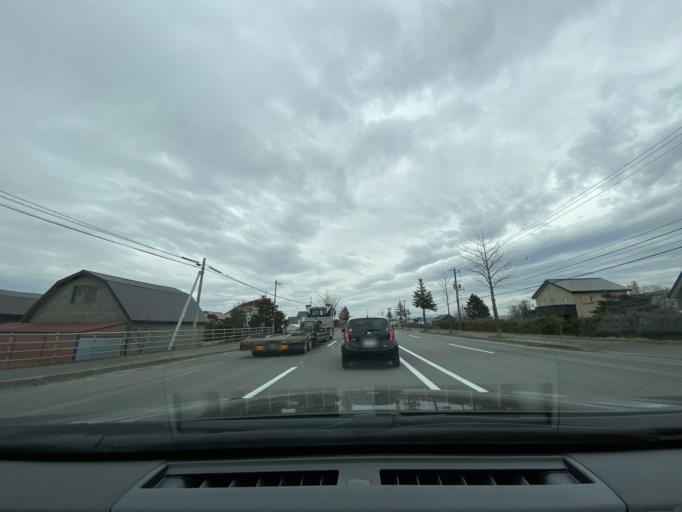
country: JP
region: Hokkaido
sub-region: Asahikawa-shi
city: Asahikawa
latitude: 43.8359
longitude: 142.4745
